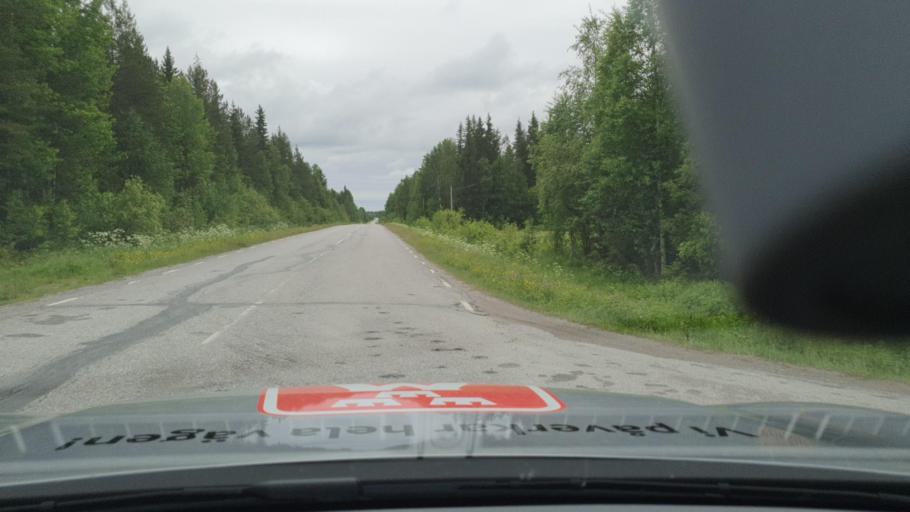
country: SE
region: Norrbotten
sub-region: Lulea Kommun
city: Ranea
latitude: 65.8542
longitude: 22.2376
